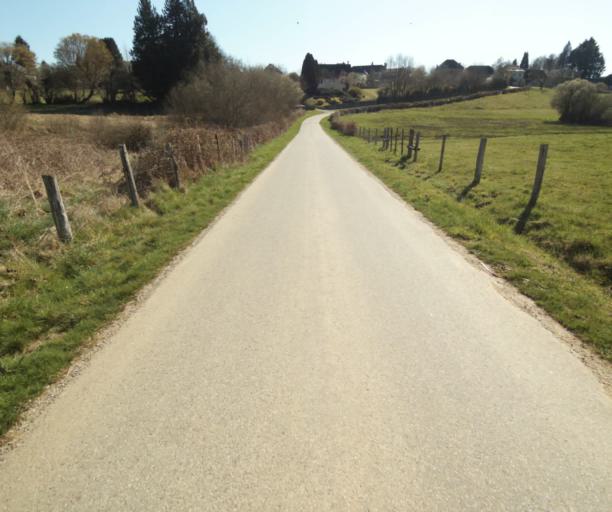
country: FR
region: Limousin
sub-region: Departement de la Correze
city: Chamboulive
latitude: 45.4684
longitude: 1.7340
